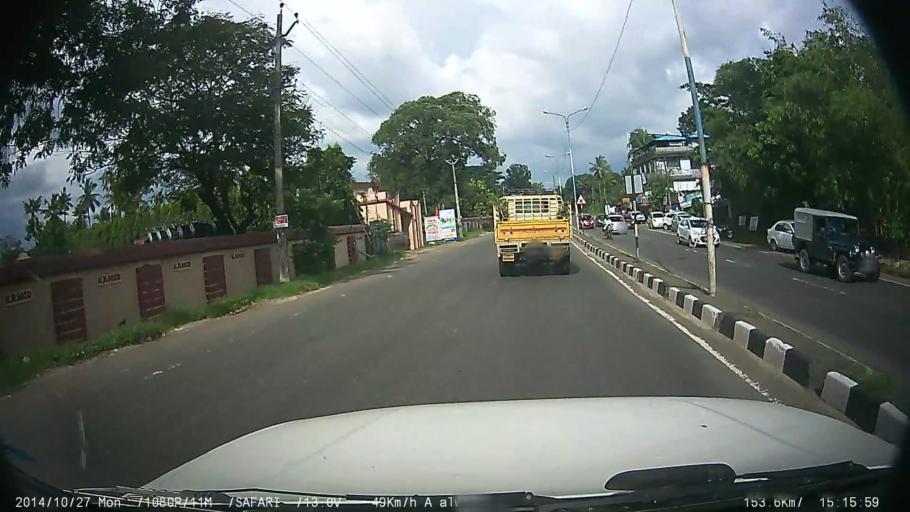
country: IN
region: Kerala
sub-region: Ernakulam
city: Aluva
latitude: 10.1569
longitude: 76.3550
